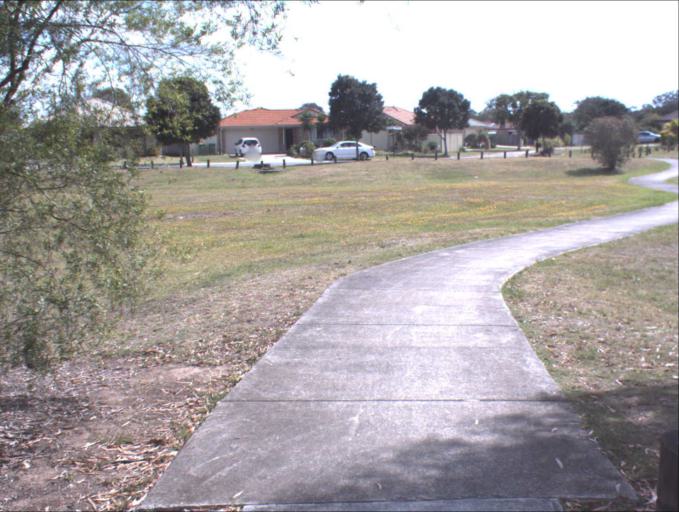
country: AU
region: Queensland
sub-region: Logan
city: Slacks Creek
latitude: -27.6599
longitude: 153.1463
